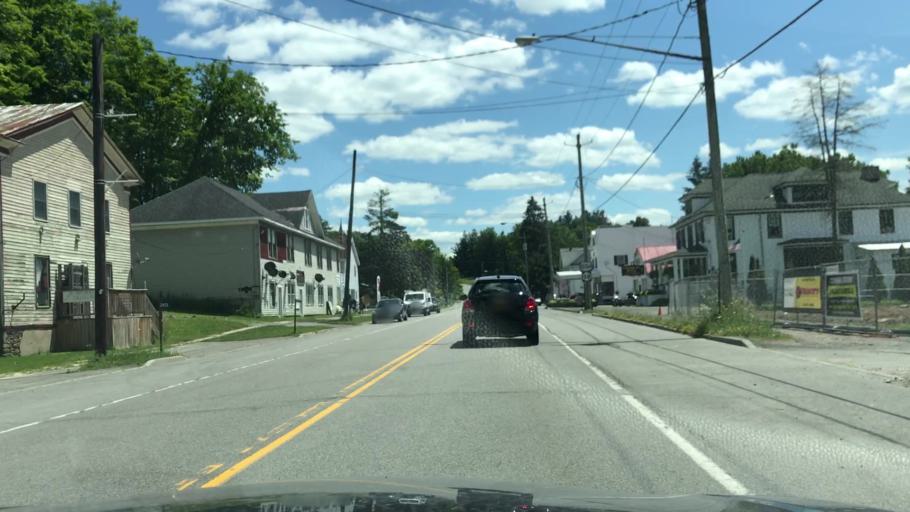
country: US
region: New York
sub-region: Wyoming County
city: Attica
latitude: 42.7617
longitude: -78.3130
